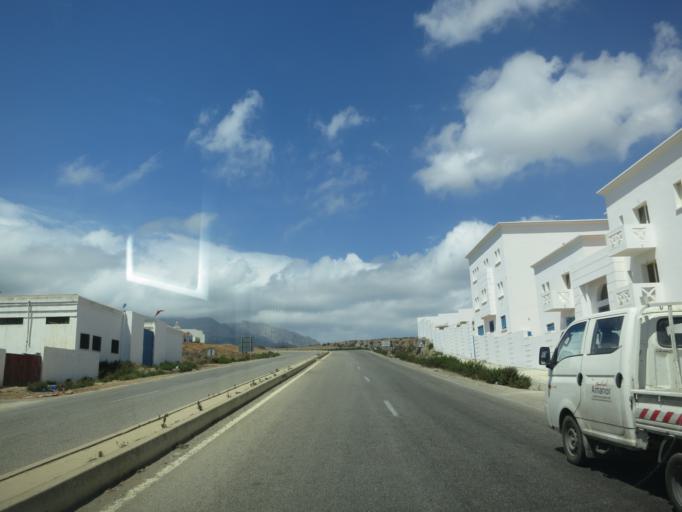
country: ES
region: Ceuta
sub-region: Ceuta
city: Ceuta
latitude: 35.8666
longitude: -5.3567
